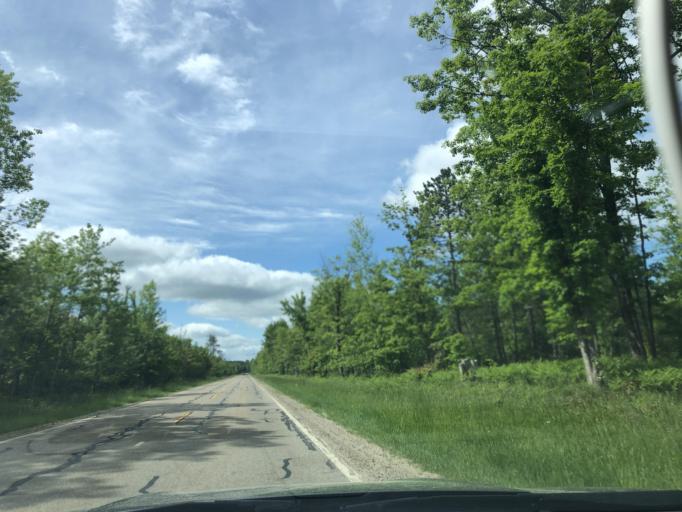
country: US
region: Michigan
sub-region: Roscommon County
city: Houghton Lake
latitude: 44.3453
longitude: -84.8546
